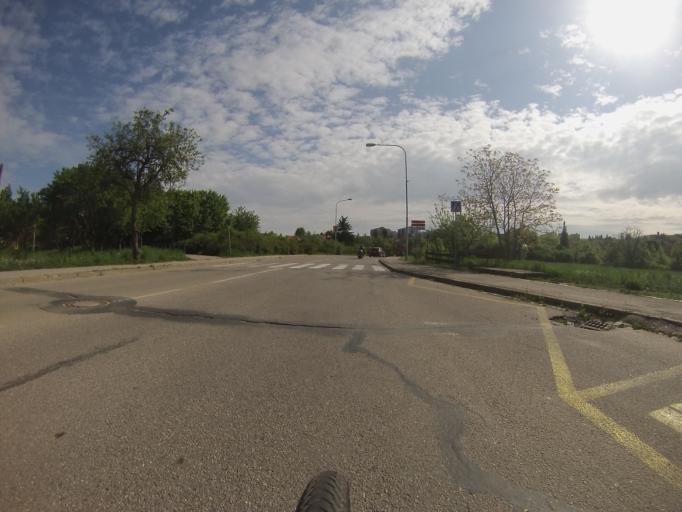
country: CZ
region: South Moravian
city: Troubsko
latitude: 49.2256
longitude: 16.5183
